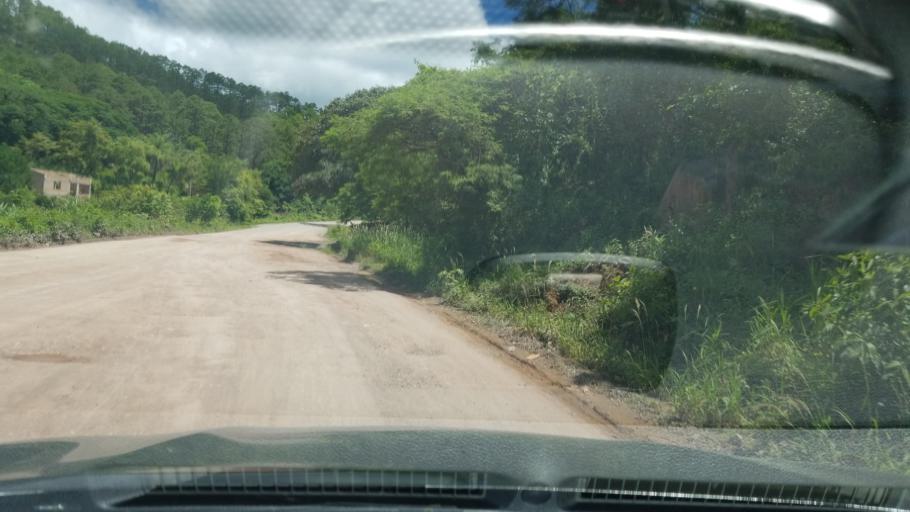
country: HN
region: Francisco Morazan
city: Talanga
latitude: 14.3533
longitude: -87.0428
